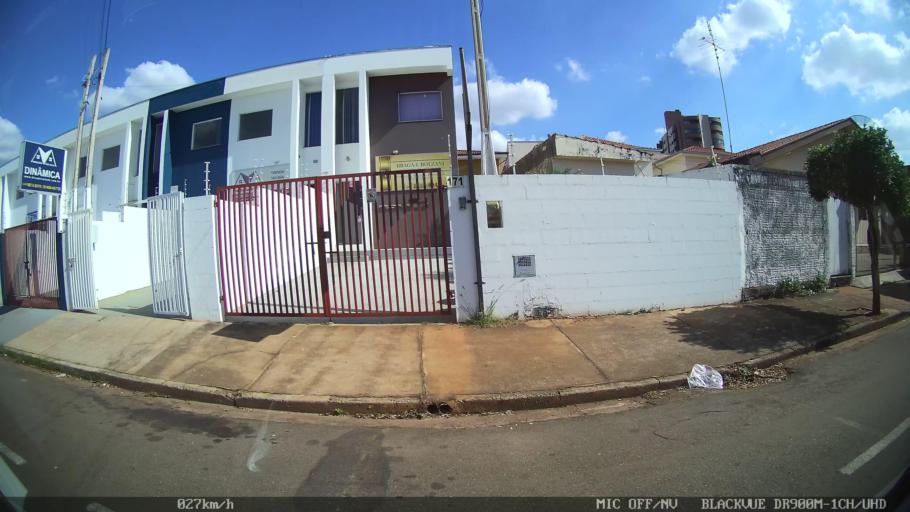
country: BR
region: Sao Paulo
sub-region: Sumare
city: Sumare
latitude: -22.8269
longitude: -47.2636
